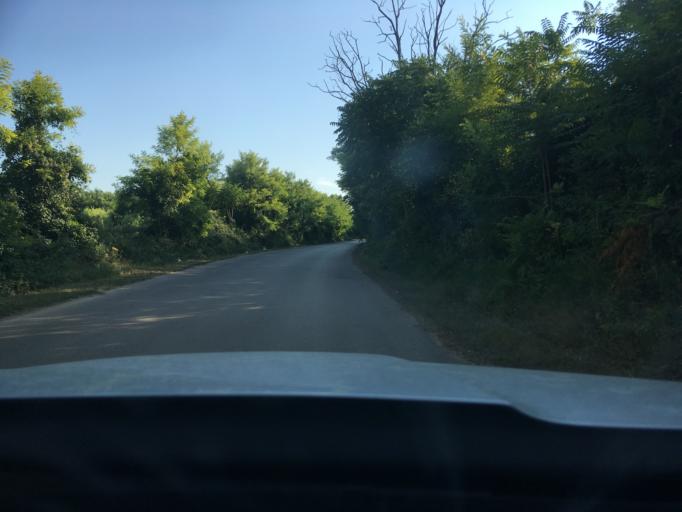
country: HR
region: Zadarska
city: Privlaka
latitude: 44.2494
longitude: 15.1500
